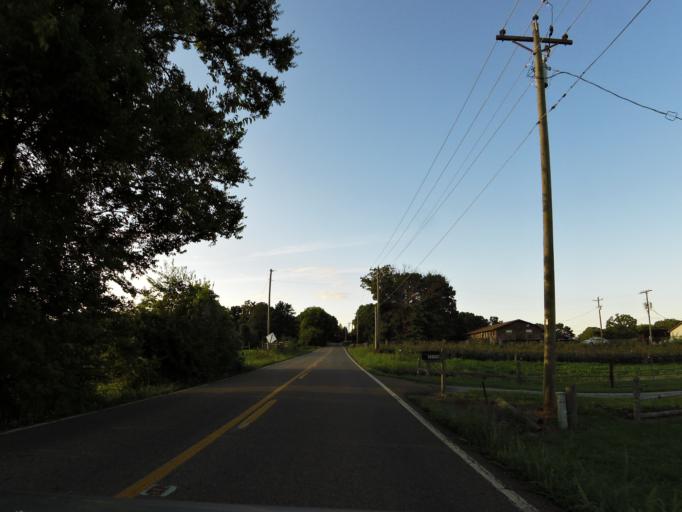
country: US
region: Tennessee
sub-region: Loudon County
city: Greenback
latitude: 35.7222
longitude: -84.2113
